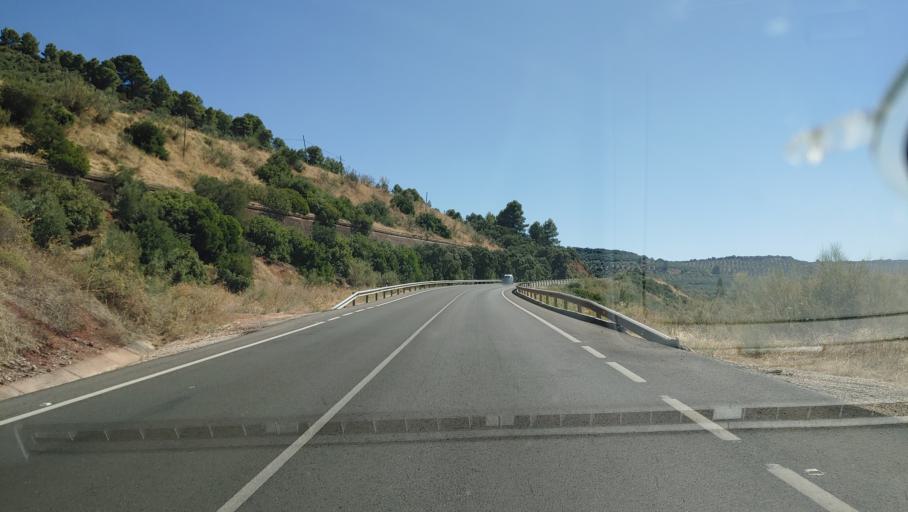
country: ES
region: Andalusia
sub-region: Provincia de Jaen
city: Campina
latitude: 38.2472
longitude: -2.9651
